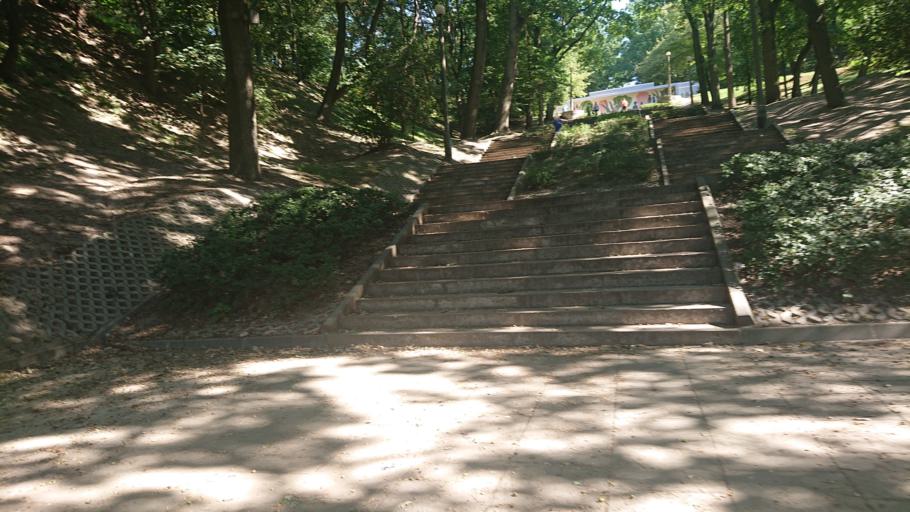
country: PL
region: Masovian Voivodeship
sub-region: Plock
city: Plock
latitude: 52.5398
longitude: 19.6904
